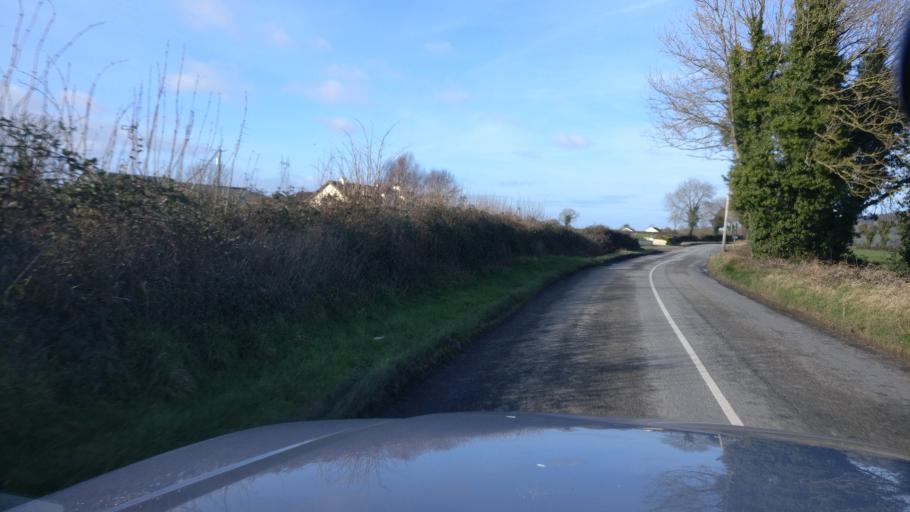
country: IE
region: Leinster
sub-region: Laois
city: Stradbally
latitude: 52.9884
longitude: -7.2195
